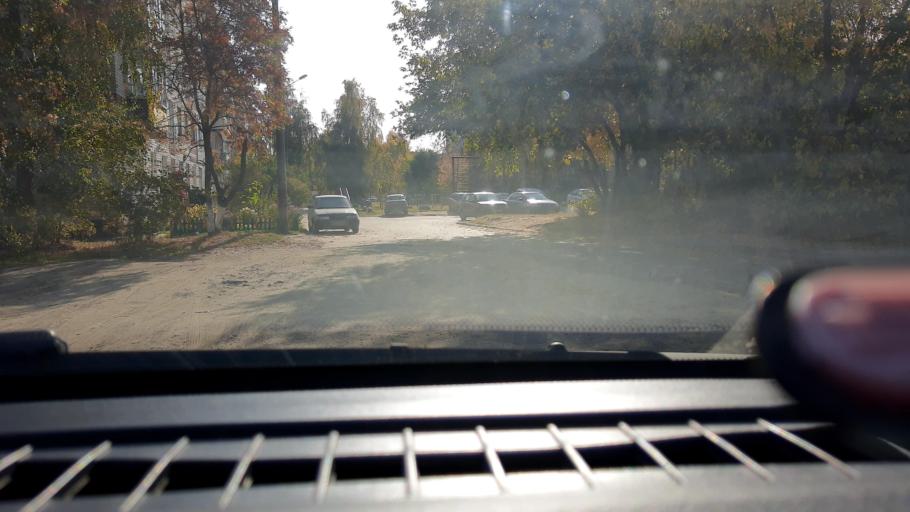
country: RU
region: Nizjnij Novgorod
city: Burevestnik
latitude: 56.2032
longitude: 43.8099
